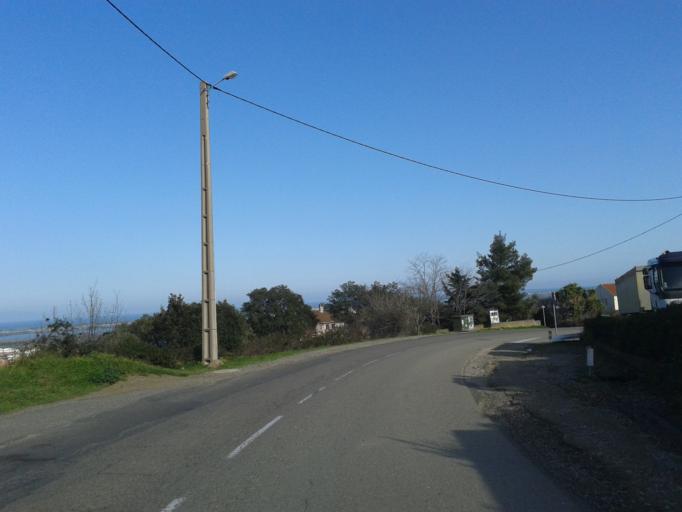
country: FR
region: Corsica
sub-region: Departement de la Haute-Corse
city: Biguglia
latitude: 42.5938
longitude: 9.4273
